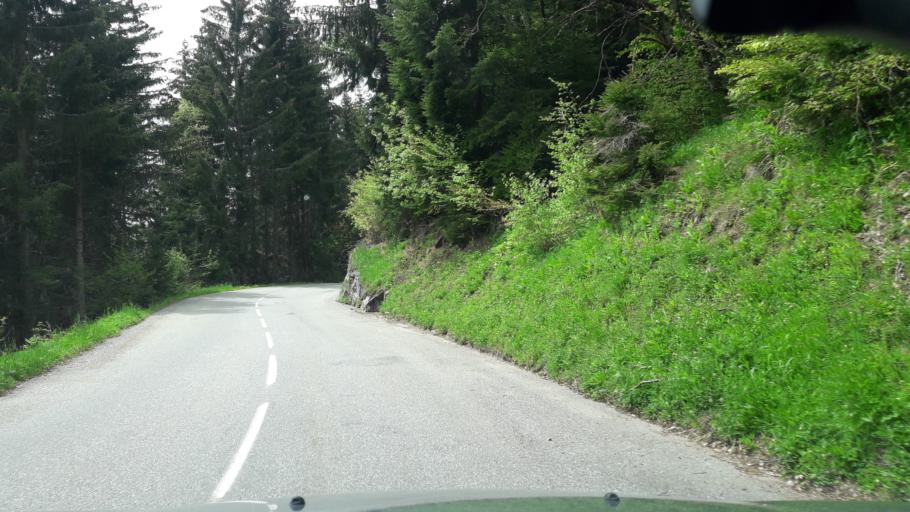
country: FR
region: Rhone-Alpes
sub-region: Departement de l'Isere
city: Theys
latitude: 45.2107
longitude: 6.0471
